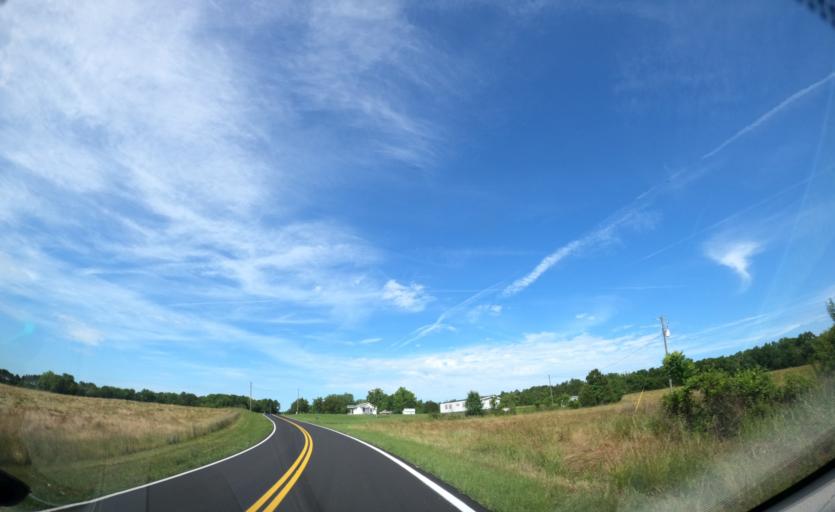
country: US
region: Georgia
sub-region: Elbert County
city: Elberton
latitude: 34.1125
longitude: -82.7460
